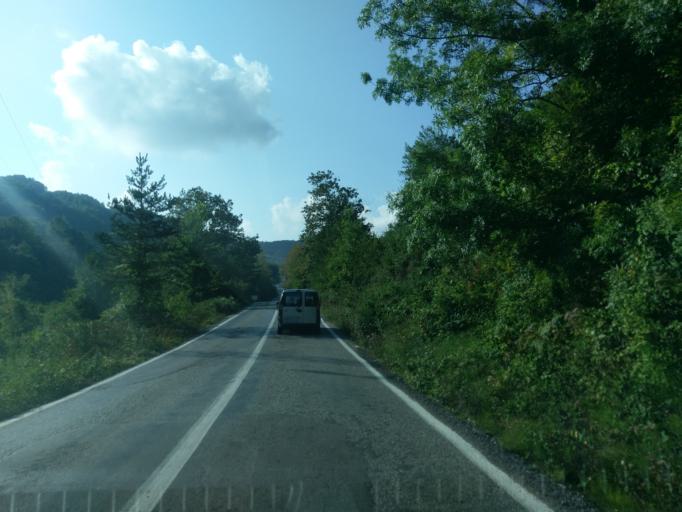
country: TR
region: Sinop
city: Ayancik
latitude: 41.8802
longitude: 34.5263
